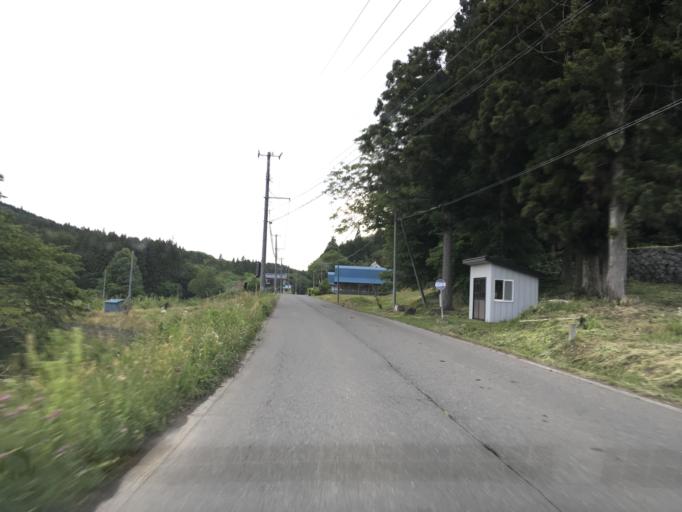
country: JP
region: Iwate
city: Mizusawa
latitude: 39.1648
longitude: 141.3084
